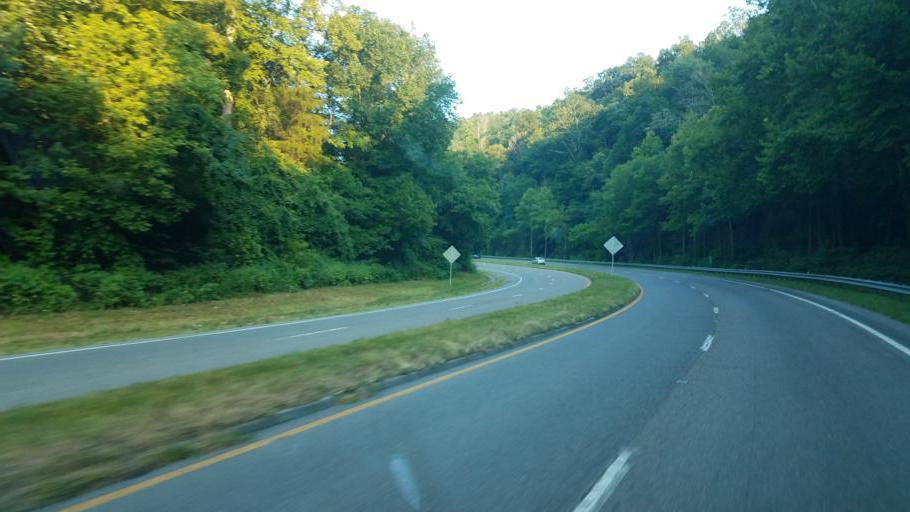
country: US
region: Tennessee
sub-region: Hawkins County
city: Church Hill
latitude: 36.6465
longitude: -82.7488
